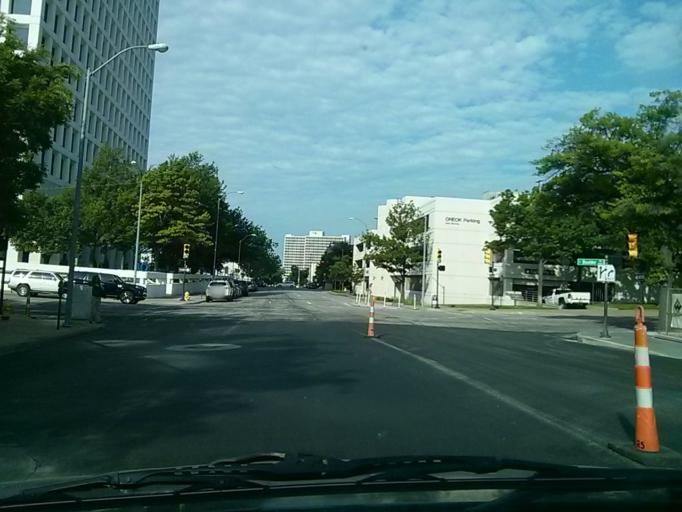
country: US
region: Oklahoma
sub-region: Tulsa County
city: Tulsa
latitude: 36.1493
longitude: -95.9897
